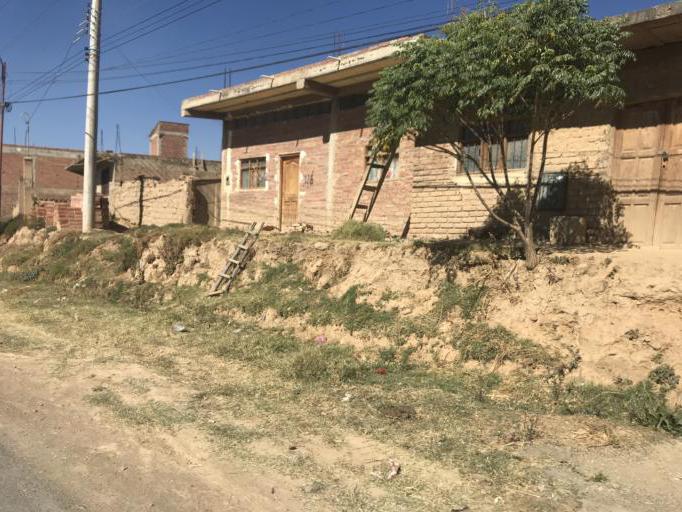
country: BO
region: Cochabamba
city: Cliza
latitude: -17.5753
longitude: -65.9039
